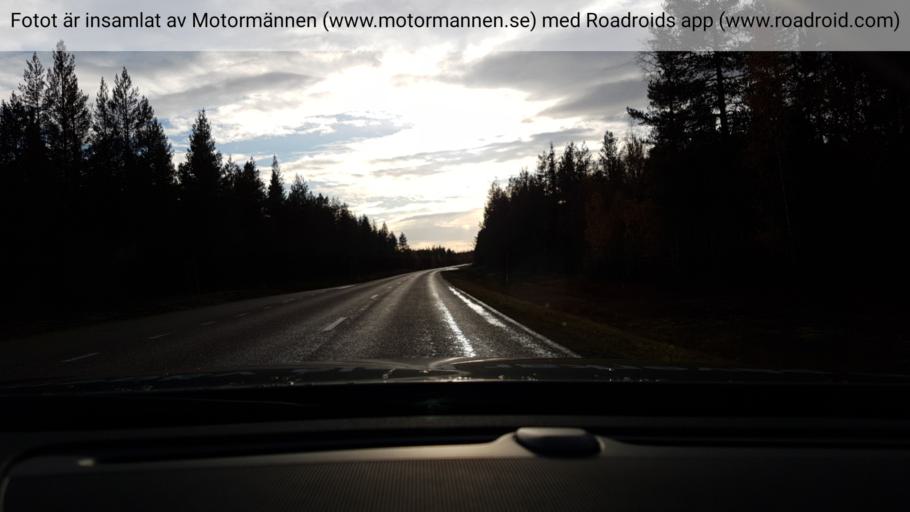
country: SE
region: Norrbotten
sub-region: Pajala Kommun
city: Pajala
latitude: 67.1713
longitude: 22.6807
